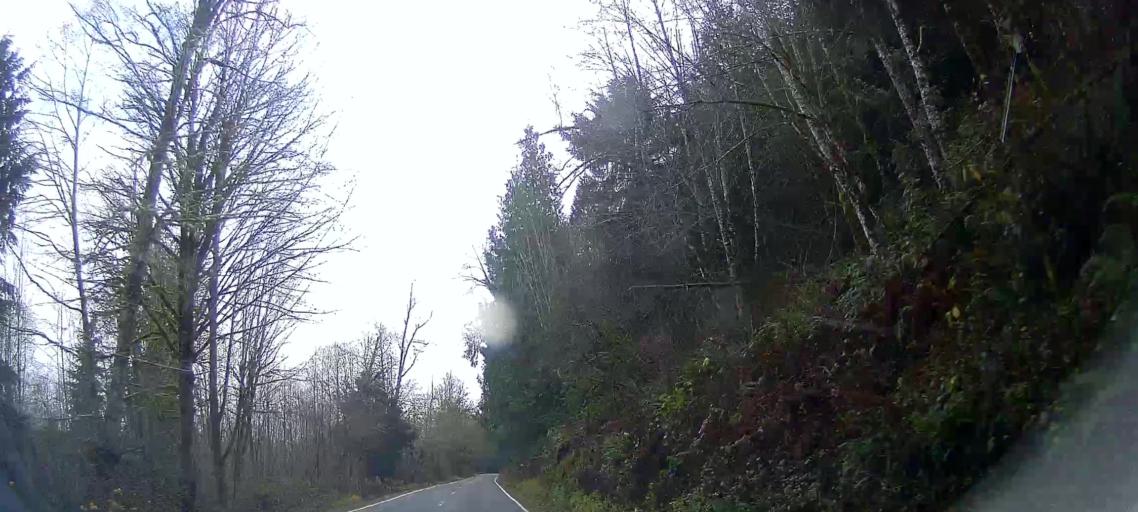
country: US
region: Washington
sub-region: Skagit County
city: Sedro-Woolley
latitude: 48.5124
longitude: -121.9339
